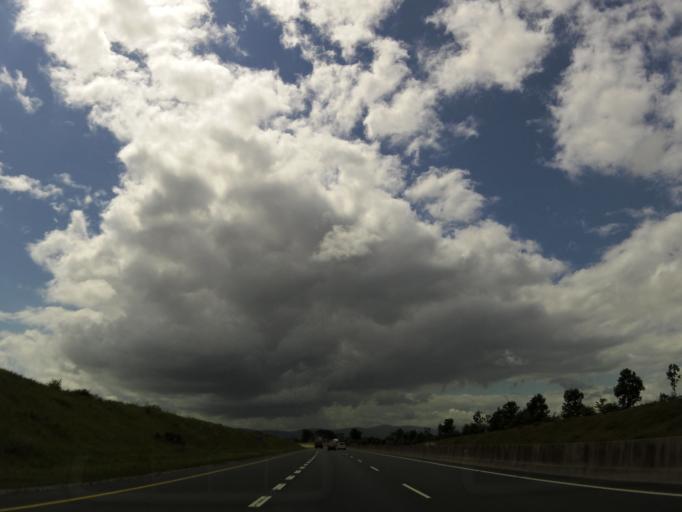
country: IE
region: Munster
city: Cashel
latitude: 52.4930
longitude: -7.8959
